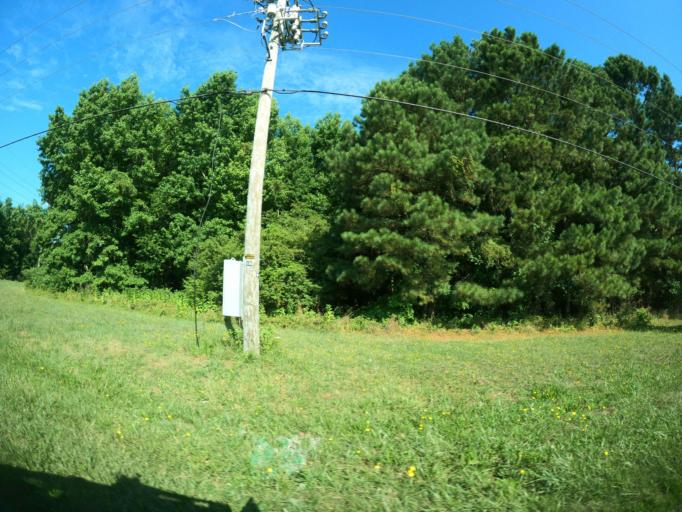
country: US
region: Delaware
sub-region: Sussex County
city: Ocean View
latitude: 38.5242
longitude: -75.0951
